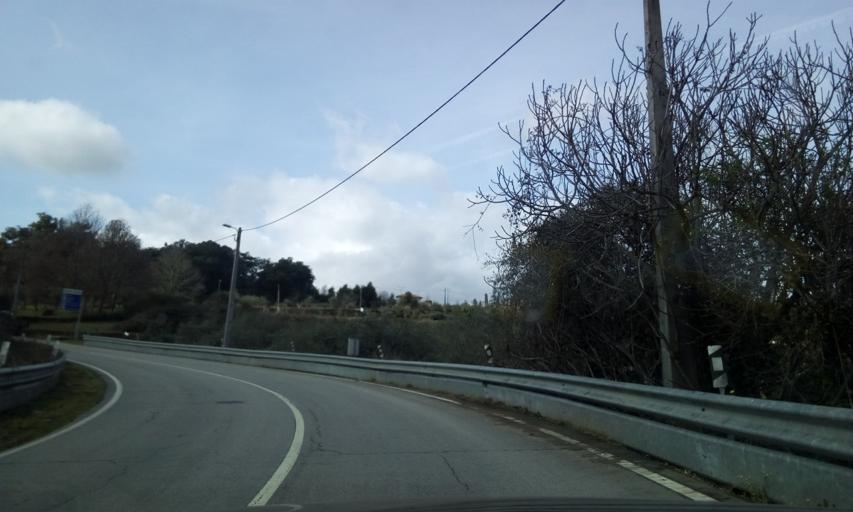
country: PT
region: Viseu
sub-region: Satao
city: Satao
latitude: 40.6717
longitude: -7.6957
